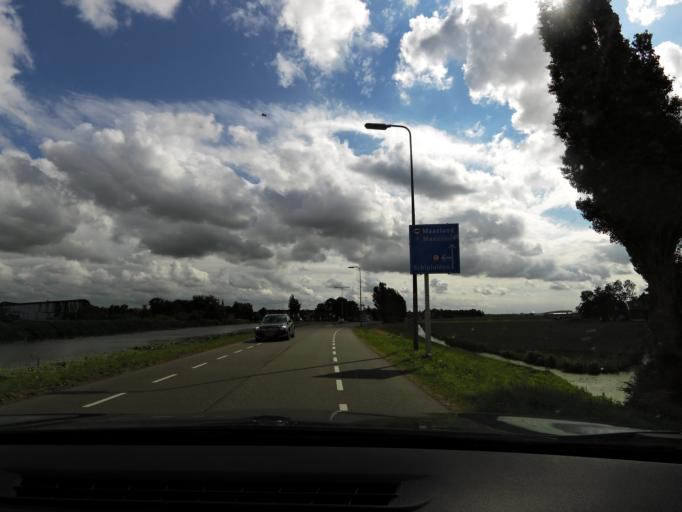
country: NL
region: South Holland
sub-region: Gemeente Delft
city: Delft
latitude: 51.9820
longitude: 4.3179
